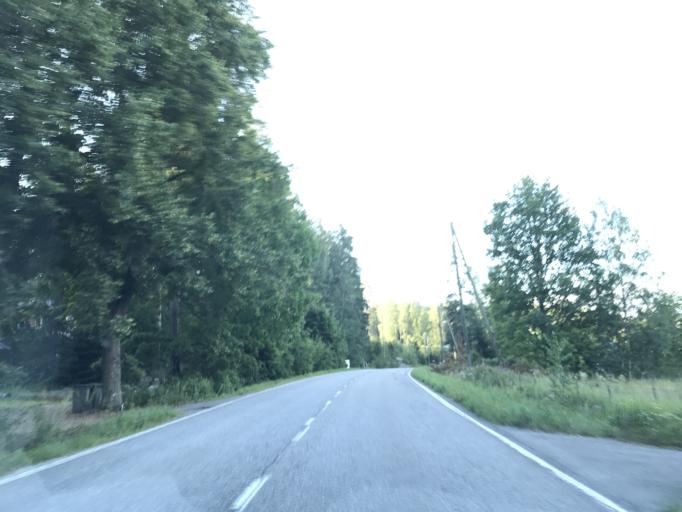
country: FI
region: Uusimaa
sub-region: Helsinki
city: Nurmijaervi
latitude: 60.3772
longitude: 24.6765
